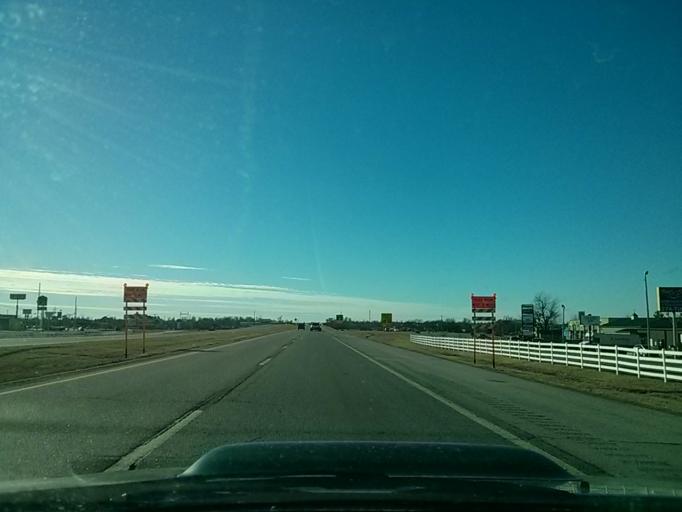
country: US
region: Oklahoma
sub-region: Tulsa County
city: Owasso
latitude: 36.2682
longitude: -95.8483
